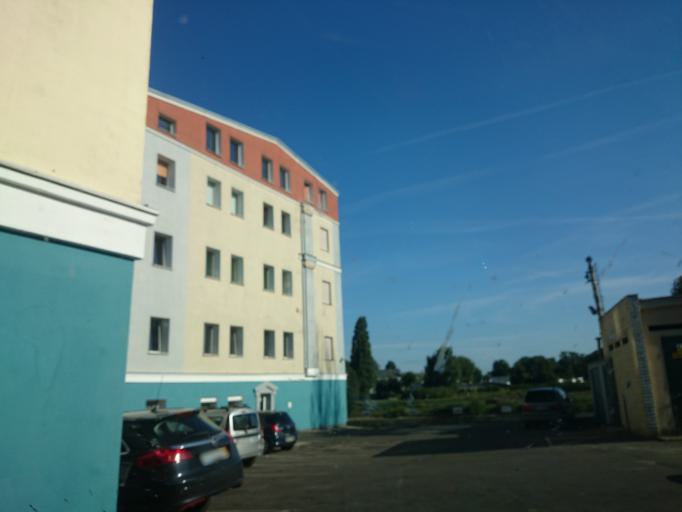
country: PL
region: Lubusz
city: Gorzow Wielkopolski
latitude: 52.7281
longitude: 15.2346
